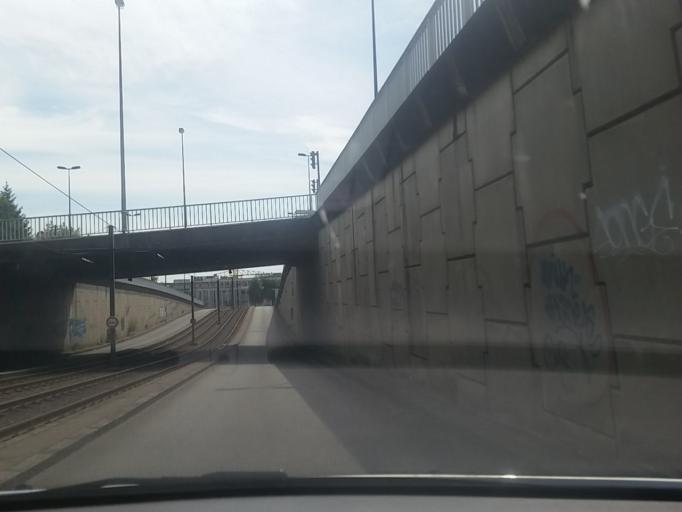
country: FR
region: Pays de la Loire
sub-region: Departement de la Loire-Atlantique
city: Nantes
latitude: 47.2071
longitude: -1.5797
